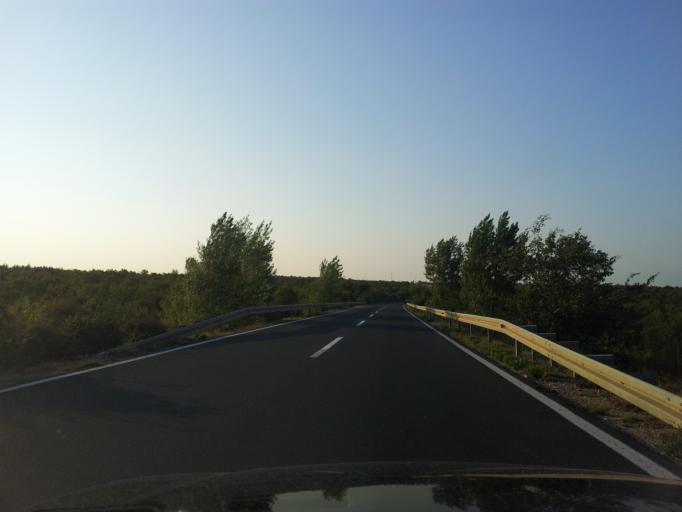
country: HR
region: Zadarska
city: Benkovac
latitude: 44.0119
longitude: 15.5725
